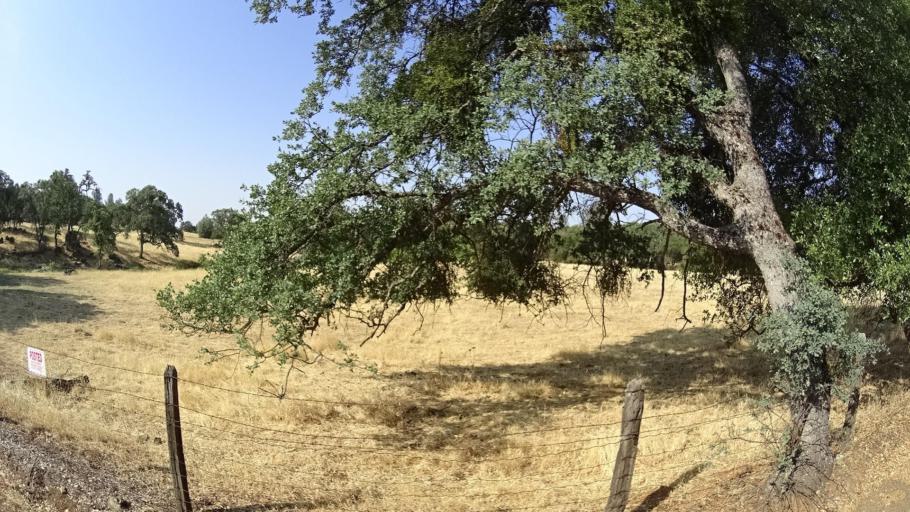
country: US
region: California
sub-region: Tuolumne County
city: Tuolumne City
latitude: 37.7156
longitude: -120.2995
